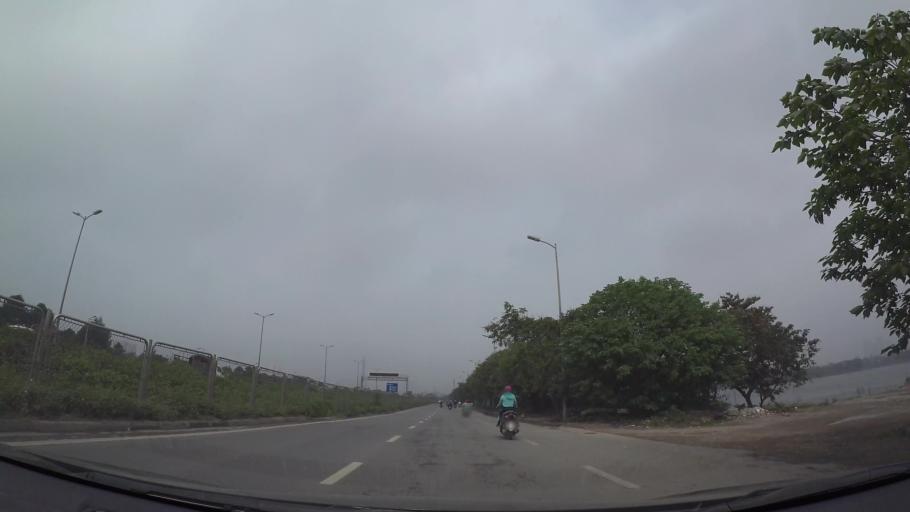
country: VN
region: Ha Noi
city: Van Dien
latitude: 20.9651
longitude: 105.8564
